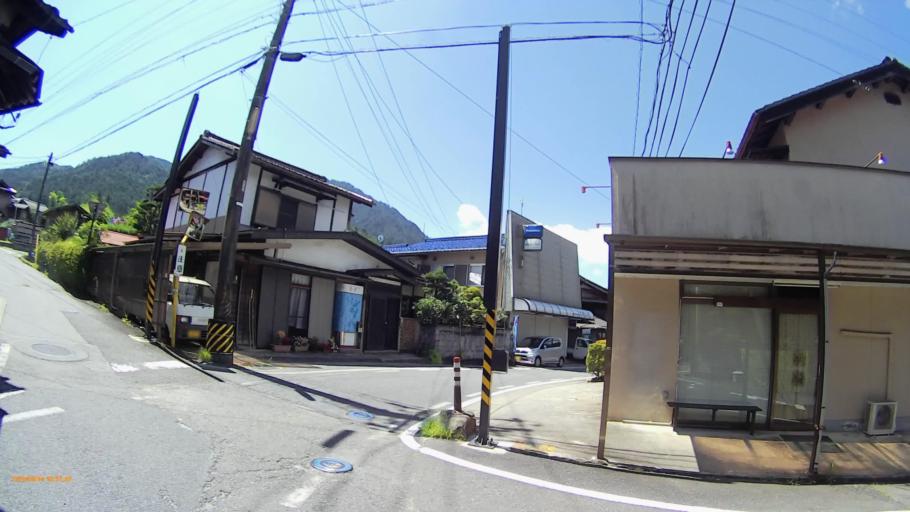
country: JP
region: Gifu
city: Nakatsugawa
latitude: 35.6715
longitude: 137.6363
